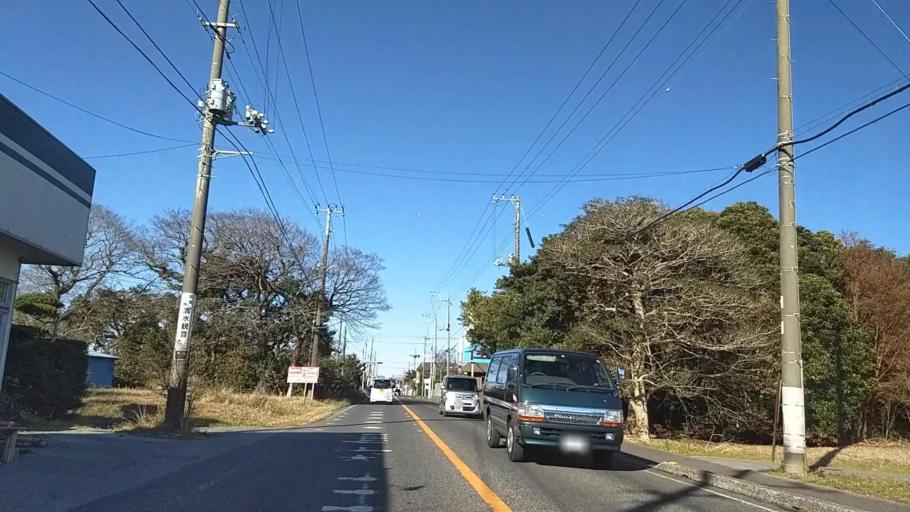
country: JP
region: Chiba
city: Ohara
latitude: 35.2823
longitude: 140.3929
